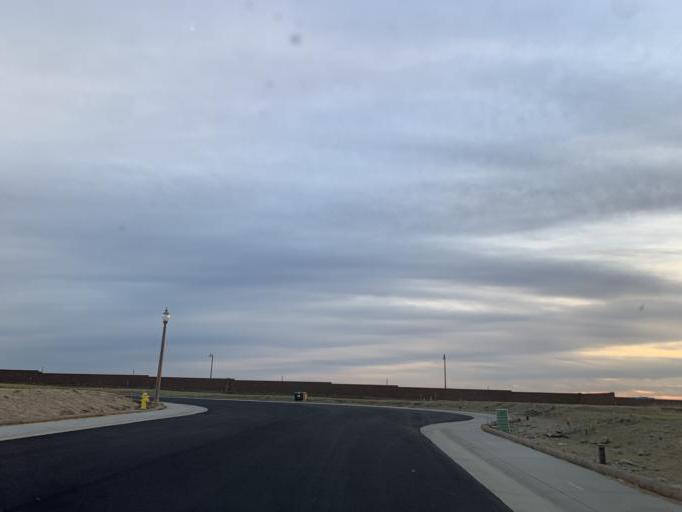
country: US
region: California
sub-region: Placer County
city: Lincoln
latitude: 38.8615
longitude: -121.2910
